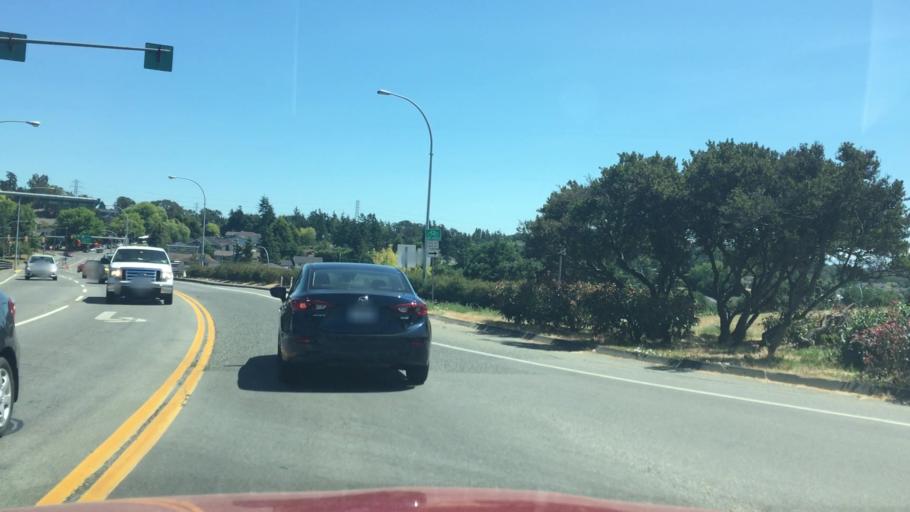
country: CA
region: British Columbia
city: Victoria
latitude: 48.4875
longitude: -123.3866
